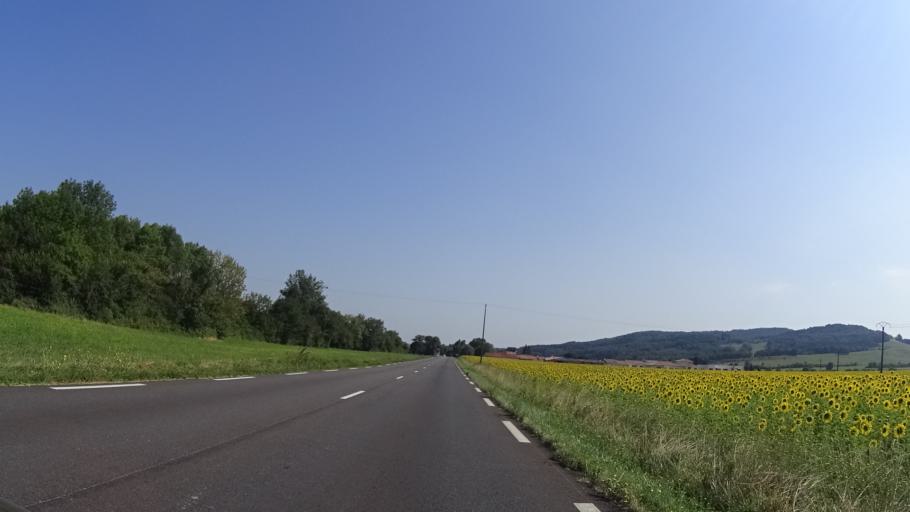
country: FR
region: Midi-Pyrenees
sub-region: Departement de l'Ariege
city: Lavelanet
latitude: 42.9907
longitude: 1.8759
